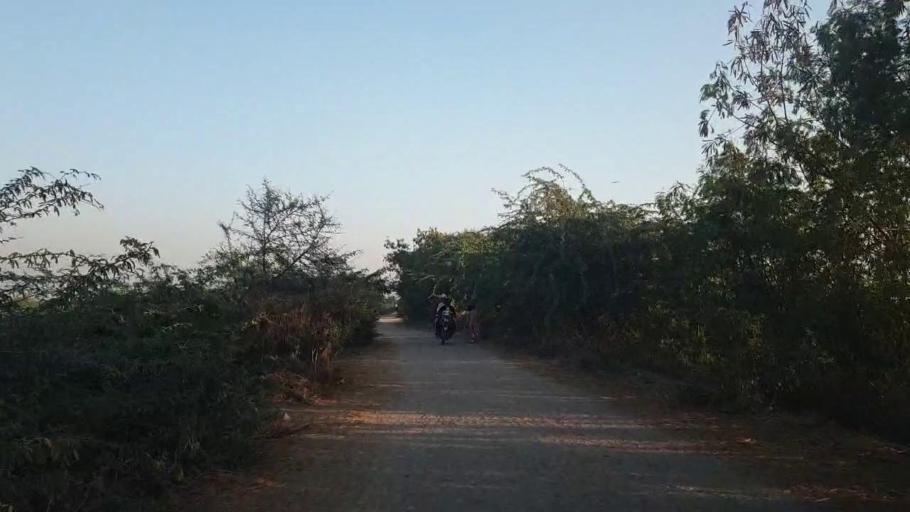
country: PK
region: Sindh
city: Mirpur Sakro
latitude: 24.4643
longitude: 67.5872
